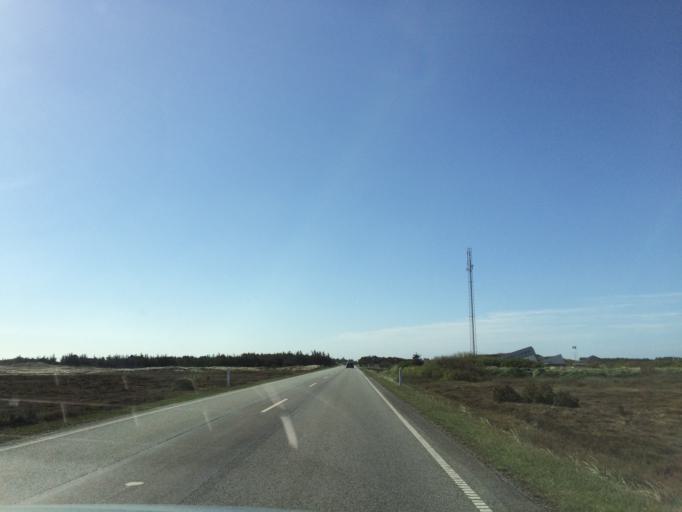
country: DK
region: Central Jutland
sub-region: Ringkobing-Skjern Kommune
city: Hvide Sande
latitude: 55.9515
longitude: 8.1510
